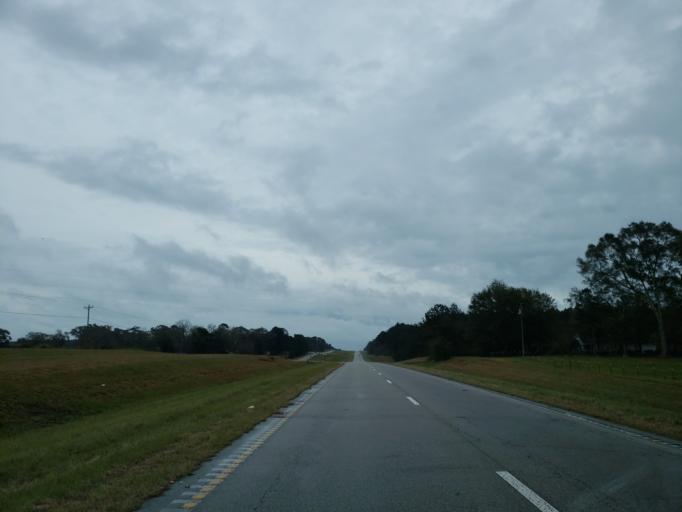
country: US
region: Mississippi
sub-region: Jones County
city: Sharon
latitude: 31.6967
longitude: -88.8867
